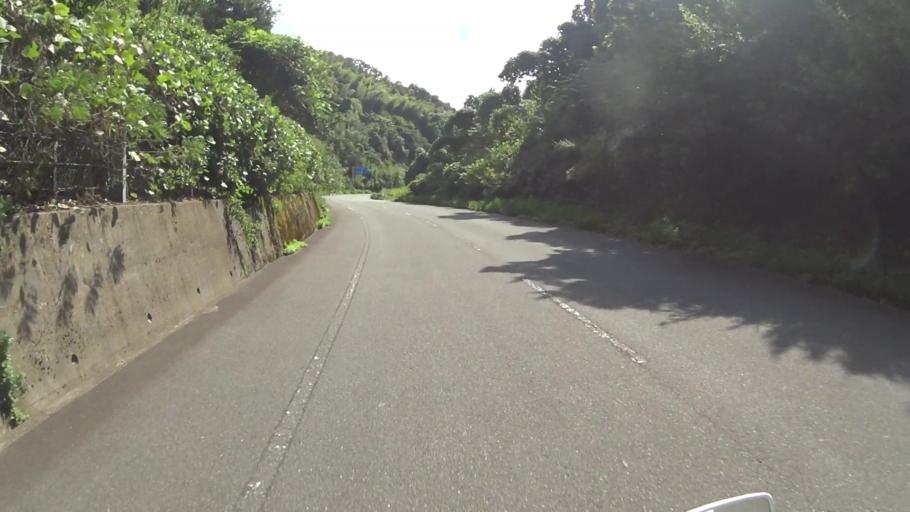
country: JP
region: Kyoto
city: Miyazu
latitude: 35.6344
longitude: 135.2099
